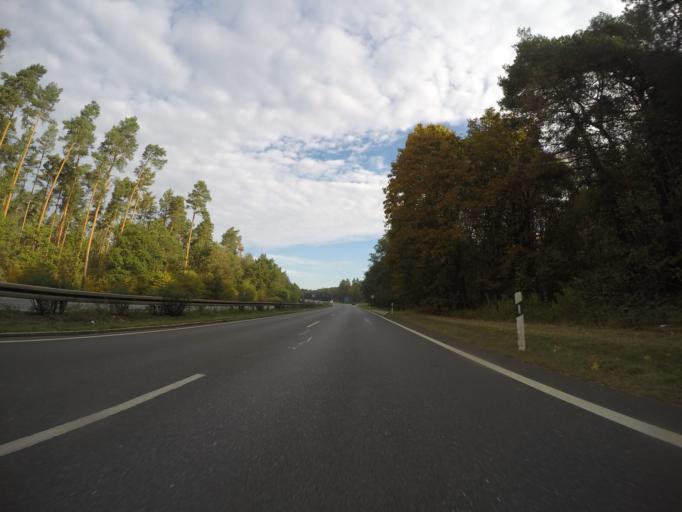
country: DE
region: Bavaria
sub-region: Regierungsbezirk Mittelfranken
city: Heroldsberg
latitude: 49.4965
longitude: 11.1334
